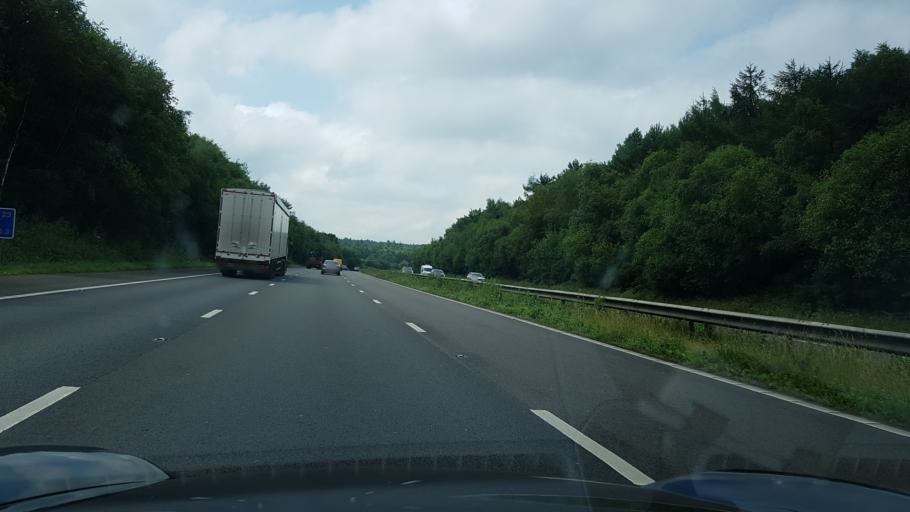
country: GB
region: England
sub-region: West Sussex
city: Maidenbower
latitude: 51.0973
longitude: -0.1538
